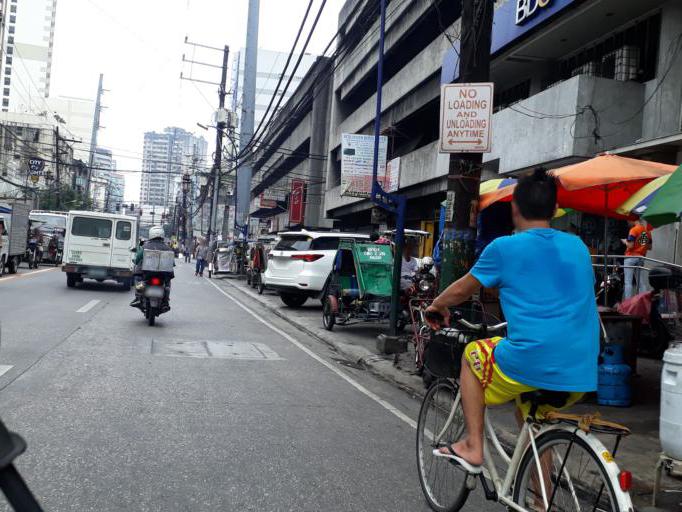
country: PH
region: Metro Manila
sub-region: City of Manila
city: Manila
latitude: 14.6061
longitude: 120.9748
